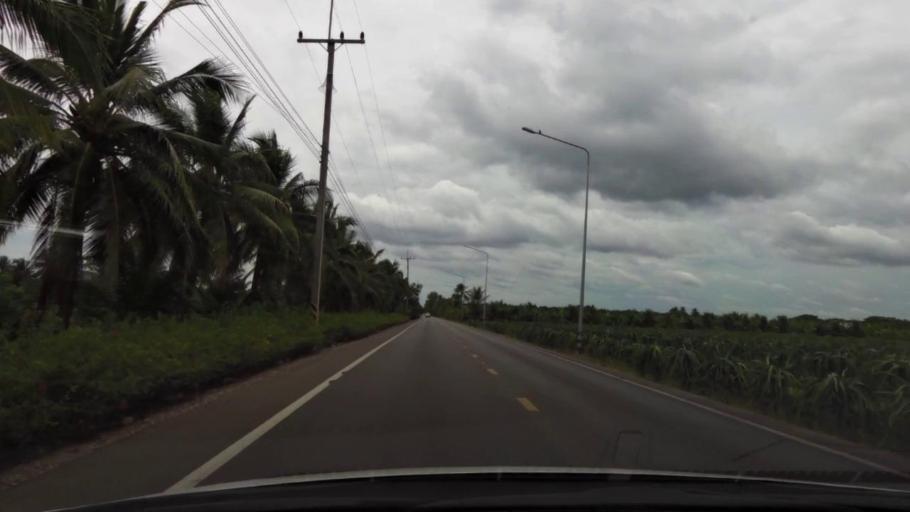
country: TH
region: Ratchaburi
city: Damnoen Saduak
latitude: 13.5583
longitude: 100.0145
